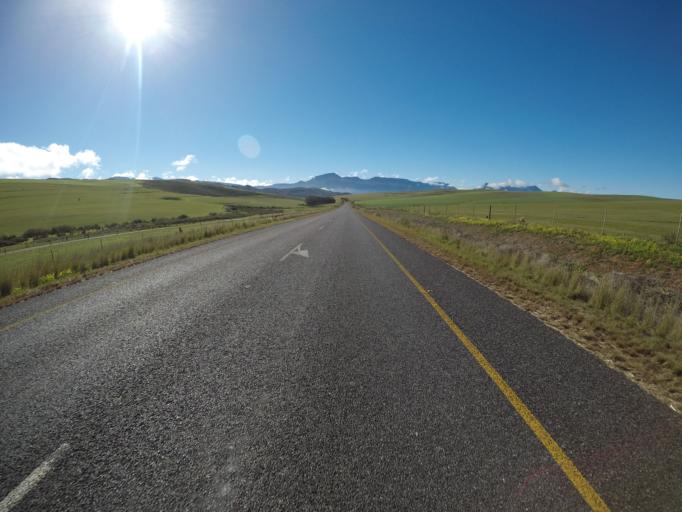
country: ZA
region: Western Cape
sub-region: Overberg District Municipality
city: Caledon
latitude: -34.1207
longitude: 19.5178
